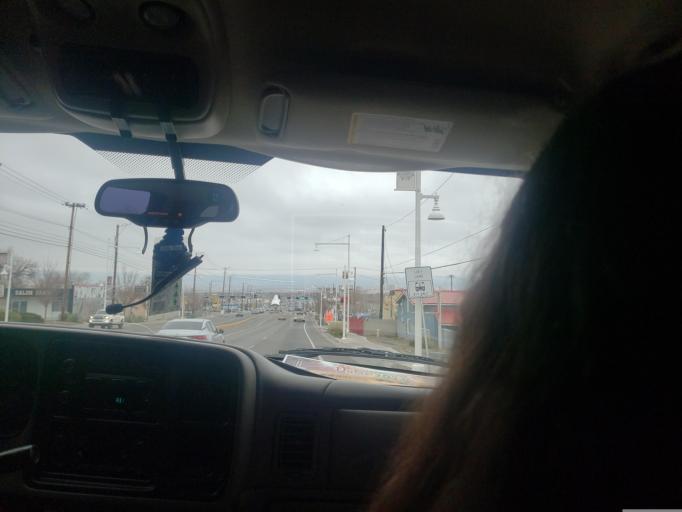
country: US
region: New Mexico
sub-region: Bernalillo County
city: Albuquerque
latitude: 35.0816
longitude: -106.7005
